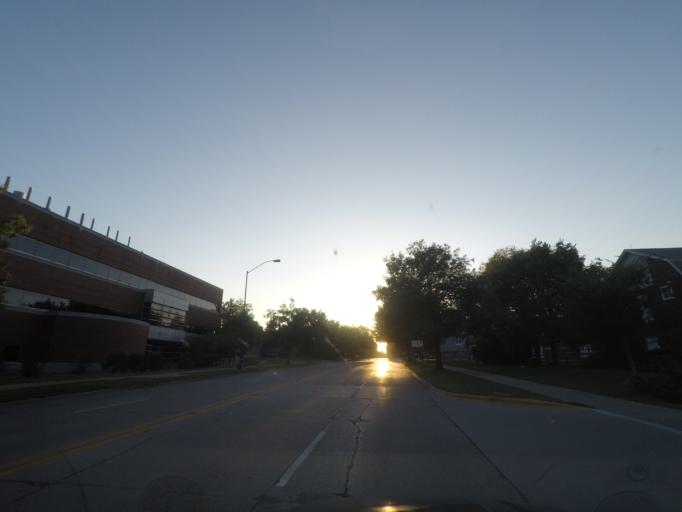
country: US
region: Iowa
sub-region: Story County
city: Ames
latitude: 42.0306
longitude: -93.6424
